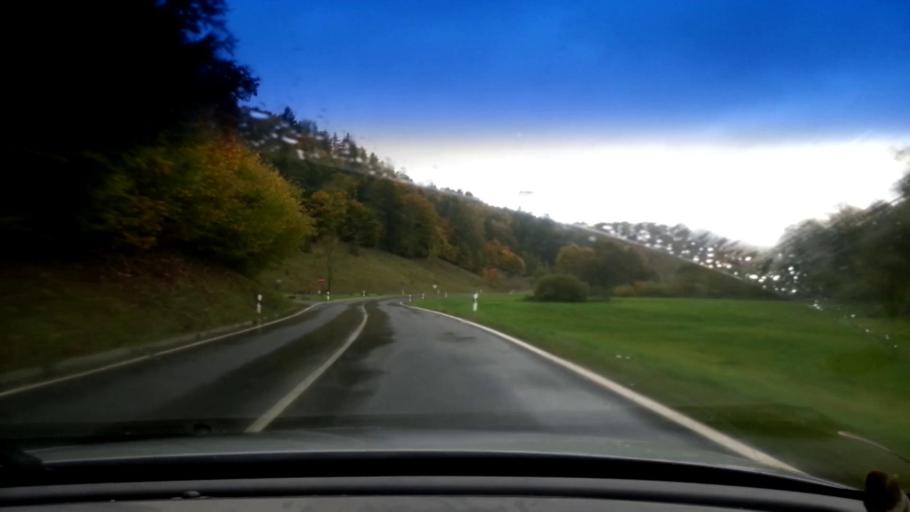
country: DE
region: Bavaria
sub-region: Upper Franconia
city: Stadelhofen
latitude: 50.0351
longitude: 11.2046
